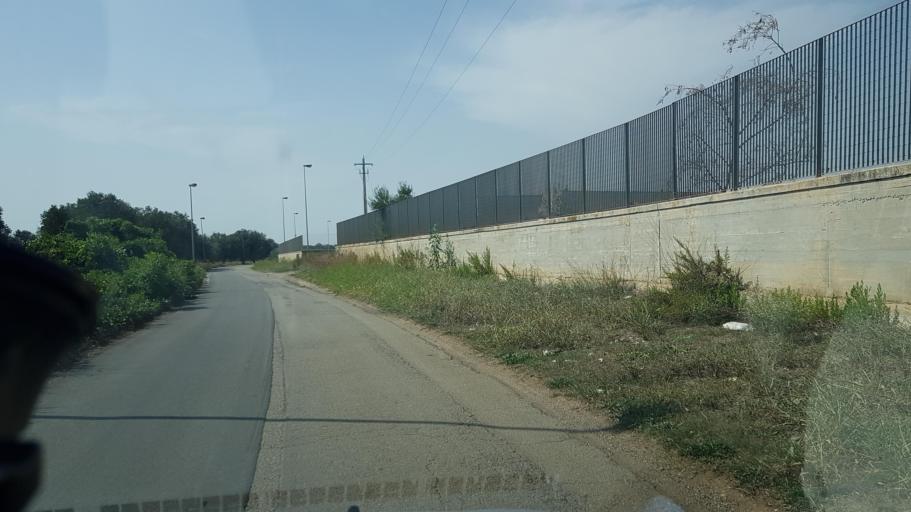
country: IT
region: Apulia
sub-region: Provincia di Brindisi
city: Mesagne
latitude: 40.5681
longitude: 17.8279
